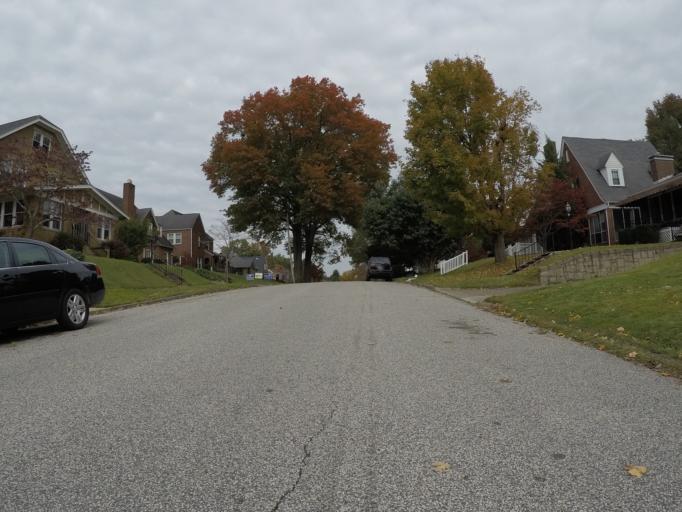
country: US
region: West Virginia
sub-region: Cabell County
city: Huntington
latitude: 38.4037
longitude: -82.4087
